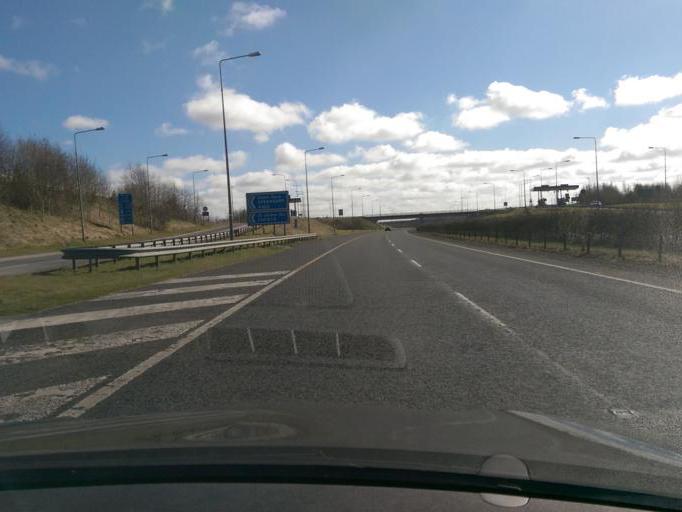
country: IE
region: Leinster
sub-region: An Mhi
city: Enfield
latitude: 53.4108
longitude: -6.8509
